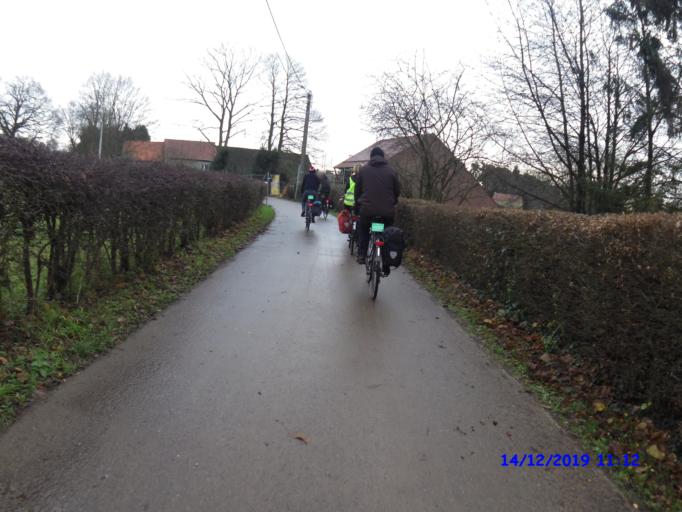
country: BE
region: Flanders
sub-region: Provincie Vlaams-Brabant
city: Beersel
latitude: 50.7490
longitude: 4.3129
